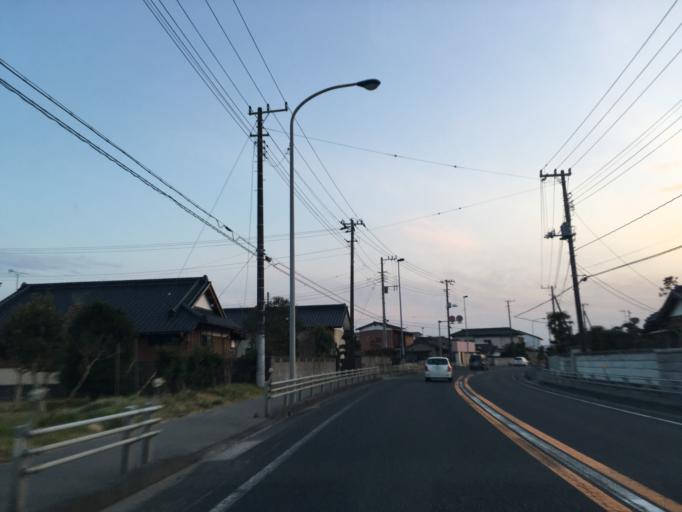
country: JP
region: Ibaraki
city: Kitaibaraki
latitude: 36.7804
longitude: 140.7444
